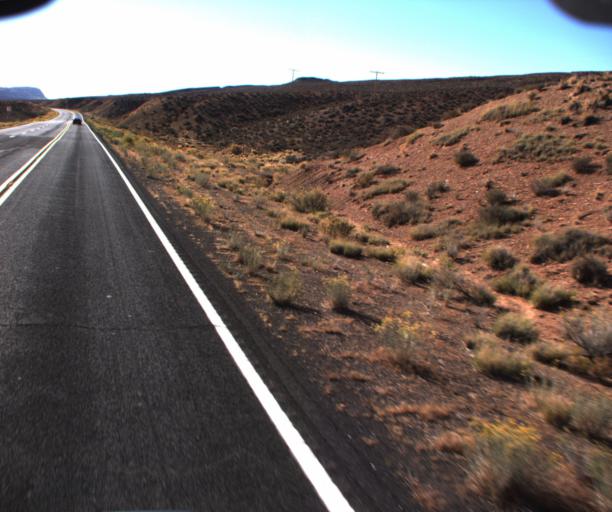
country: US
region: Arizona
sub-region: Coconino County
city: Tuba City
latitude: 36.2502
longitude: -111.4188
